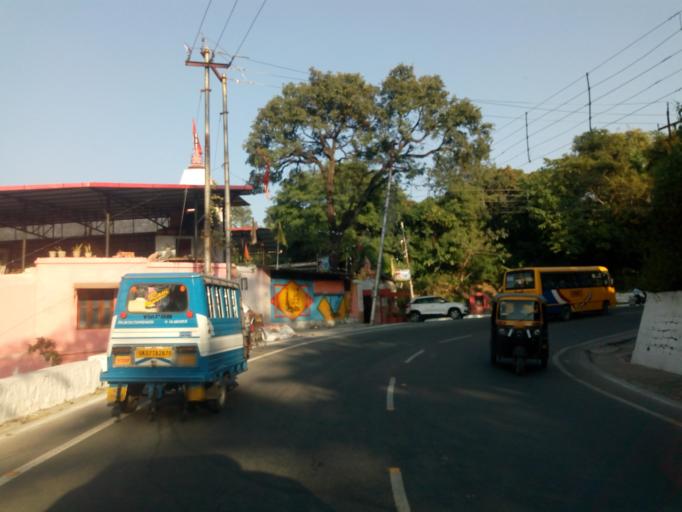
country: IN
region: Uttarakhand
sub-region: Dehradun
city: Dehradun
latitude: 30.3456
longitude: 78.0468
